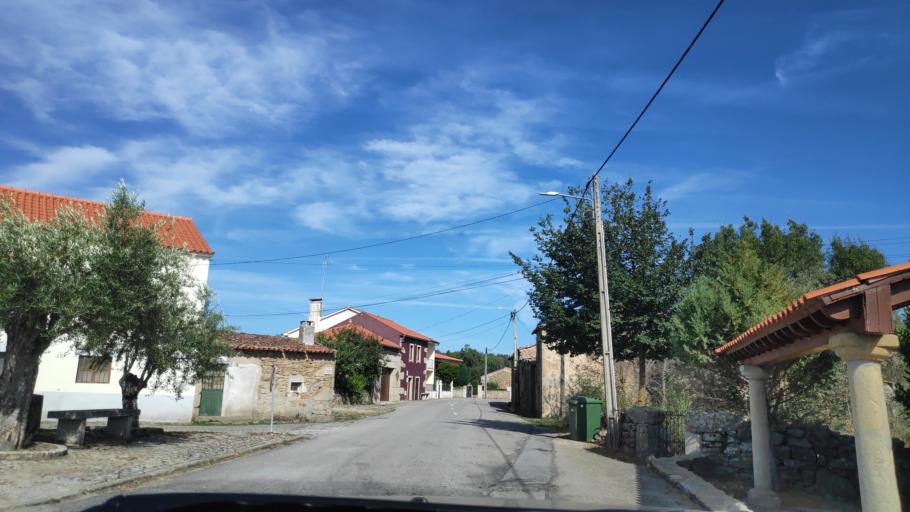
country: ES
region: Castille and Leon
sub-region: Provincia de Zamora
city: Fariza
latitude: 41.4297
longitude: -6.3461
